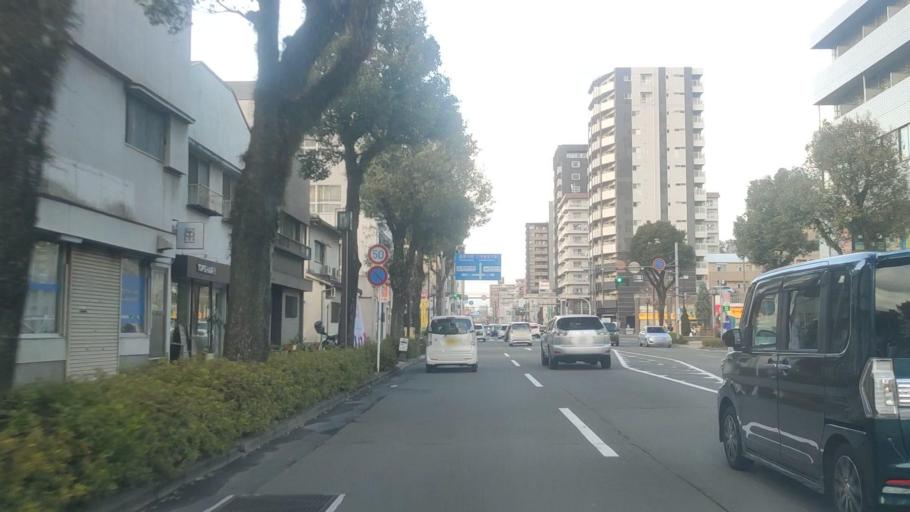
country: JP
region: Kagoshima
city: Kagoshima-shi
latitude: 31.5864
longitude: 130.5486
